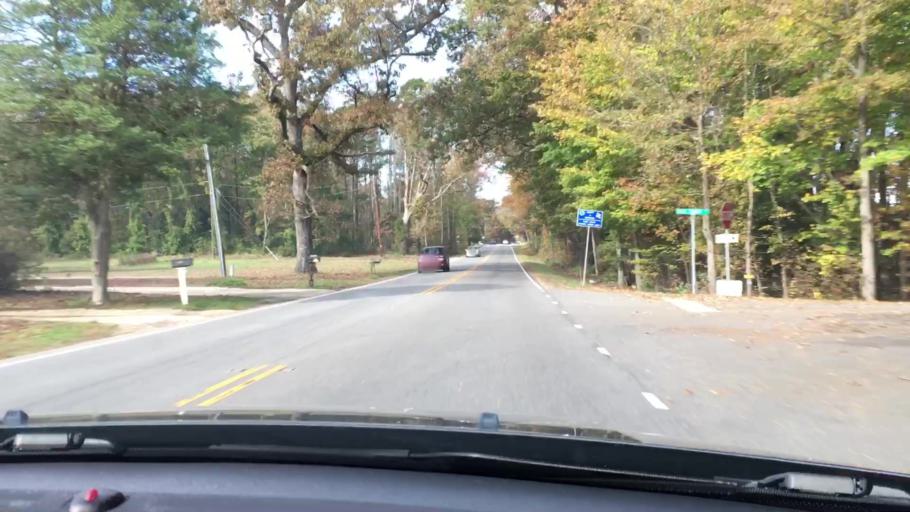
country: US
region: Virginia
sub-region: King William County
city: West Point
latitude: 37.4328
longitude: -76.8330
